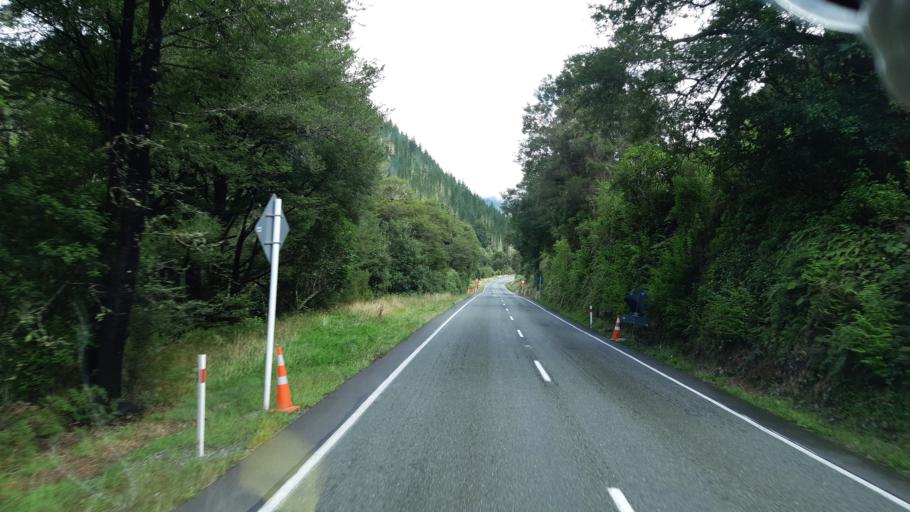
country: NZ
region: West Coast
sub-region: Buller District
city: Westport
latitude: -41.9635
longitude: 172.2017
